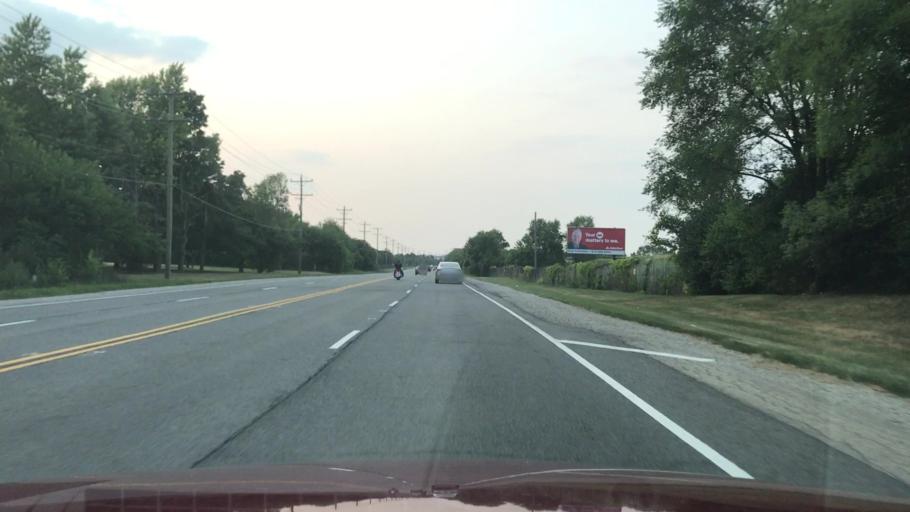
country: US
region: Illinois
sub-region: Will County
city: Lockport
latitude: 41.6126
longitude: -88.0755
